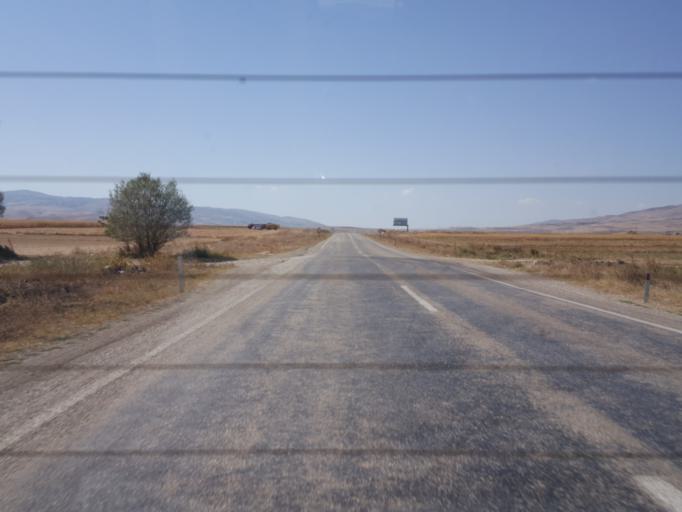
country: TR
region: Amasya
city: Dogantepe
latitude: 40.5773
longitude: 35.6182
